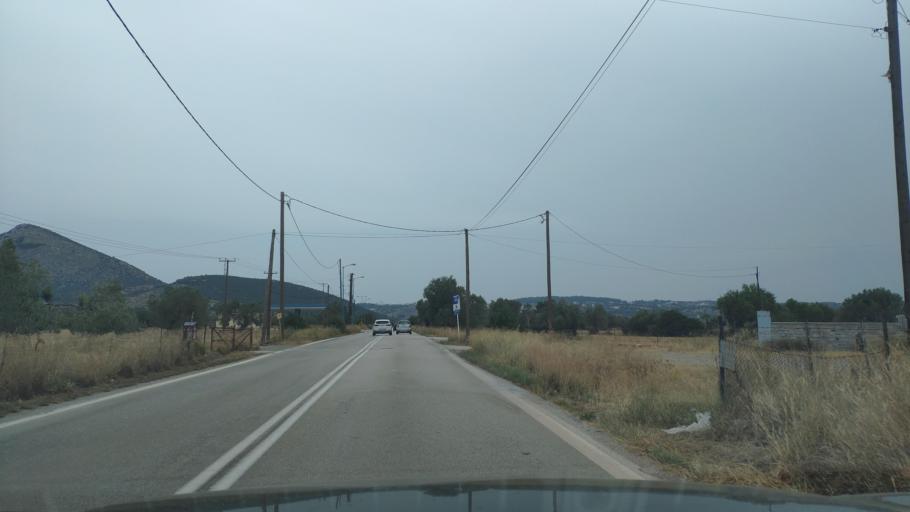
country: GR
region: Peloponnese
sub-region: Nomos Argolidos
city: Koilas
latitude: 37.4124
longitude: 23.1526
